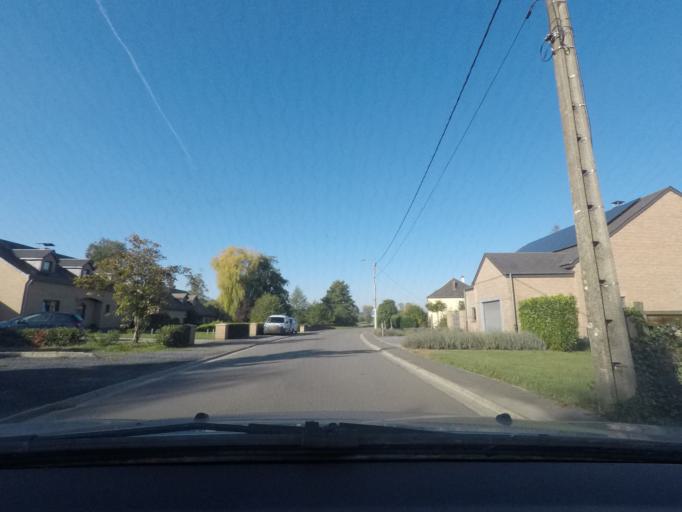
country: BE
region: Wallonia
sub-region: Province du Luxembourg
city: Messancy
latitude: 49.6301
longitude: 5.7979
